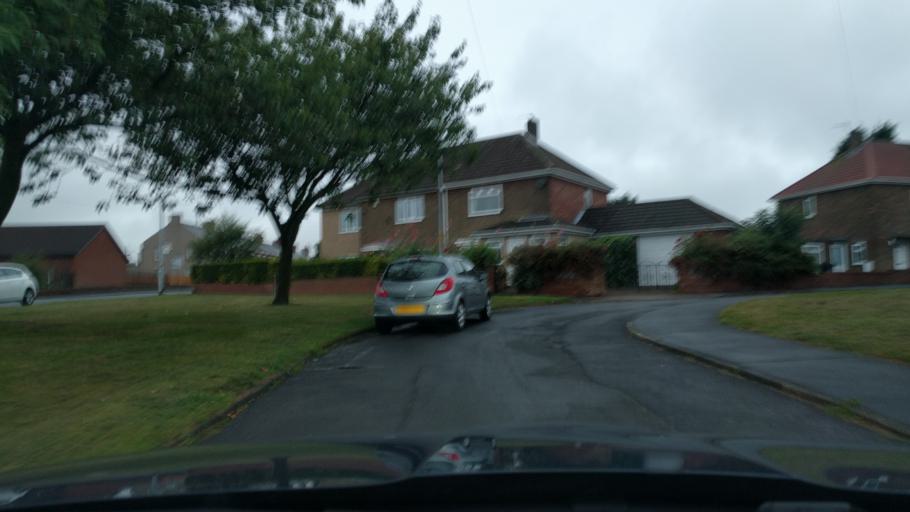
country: GB
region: England
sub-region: Northumberland
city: Bedlington
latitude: 55.1334
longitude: -1.5807
